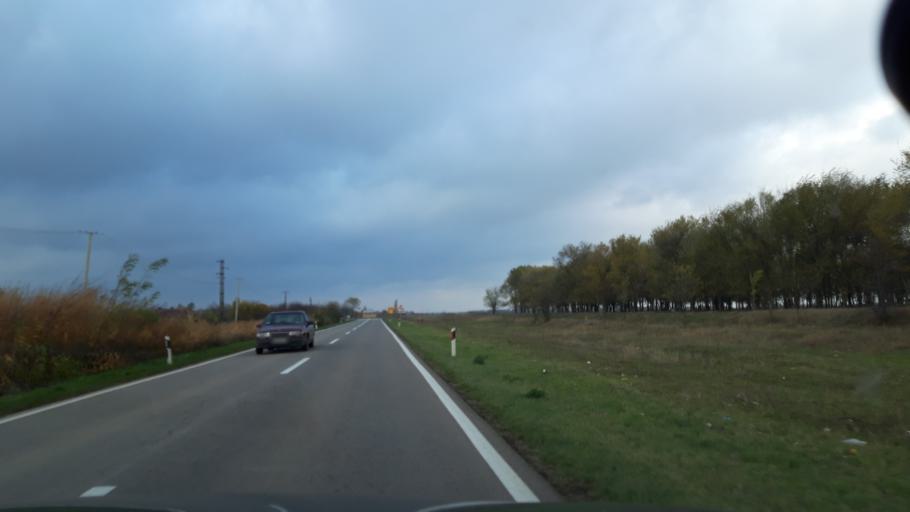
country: RS
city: Sanad
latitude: 45.9733
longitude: 20.1205
